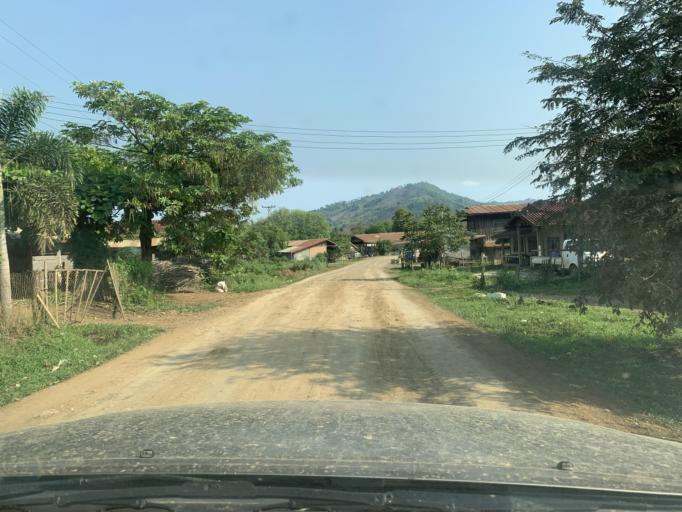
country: TH
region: Uttaradit
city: Ban Khok
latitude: 18.2906
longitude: 101.3249
